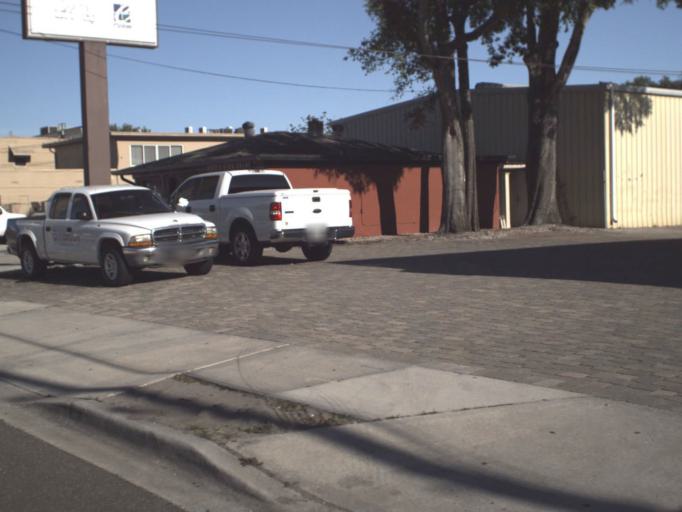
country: US
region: Florida
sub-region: Orange County
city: Fairview Shores
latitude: 28.5931
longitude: -81.3760
